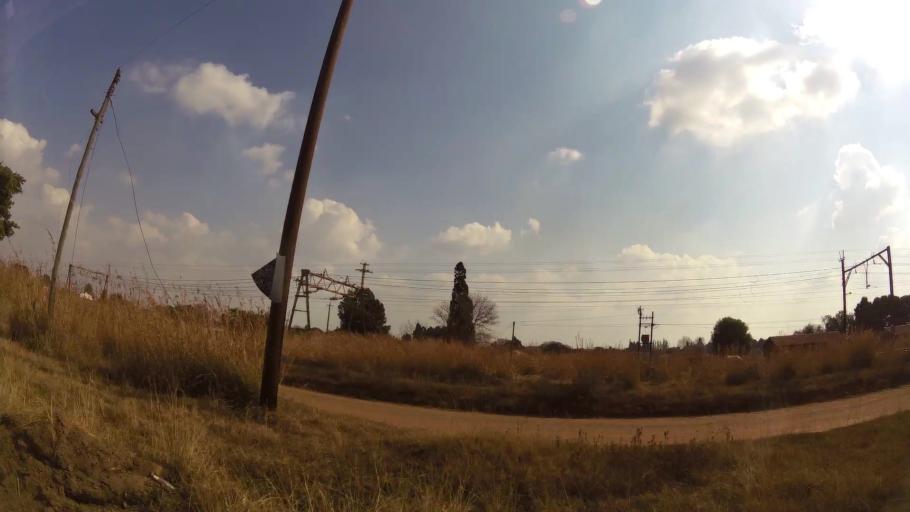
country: ZA
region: Mpumalanga
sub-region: Nkangala District Municipality
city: Delmas
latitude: -26.1908
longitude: 28.5395
